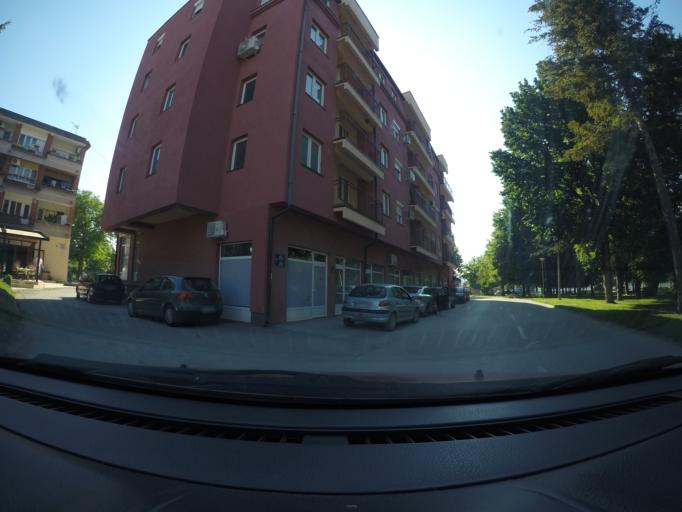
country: RS
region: Central Serbia
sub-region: Branicevski Okrug
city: Veliko Gradiste
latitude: 44.7671
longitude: 21.5188
